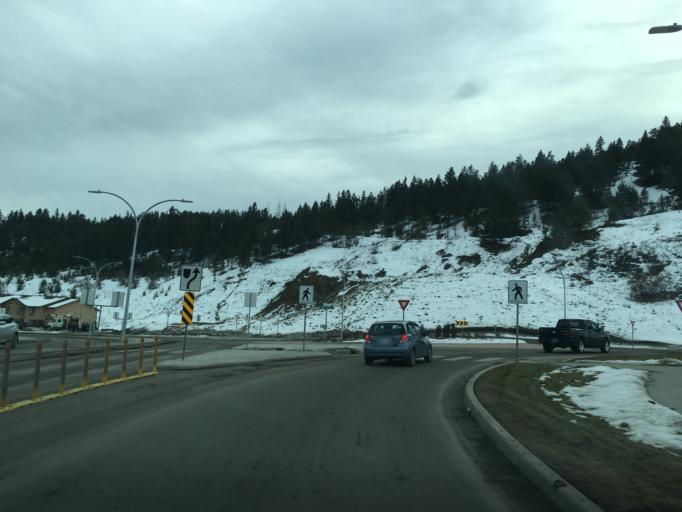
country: CA
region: British Columbia
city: Kamloops
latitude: 50.6535
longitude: -120.3831
